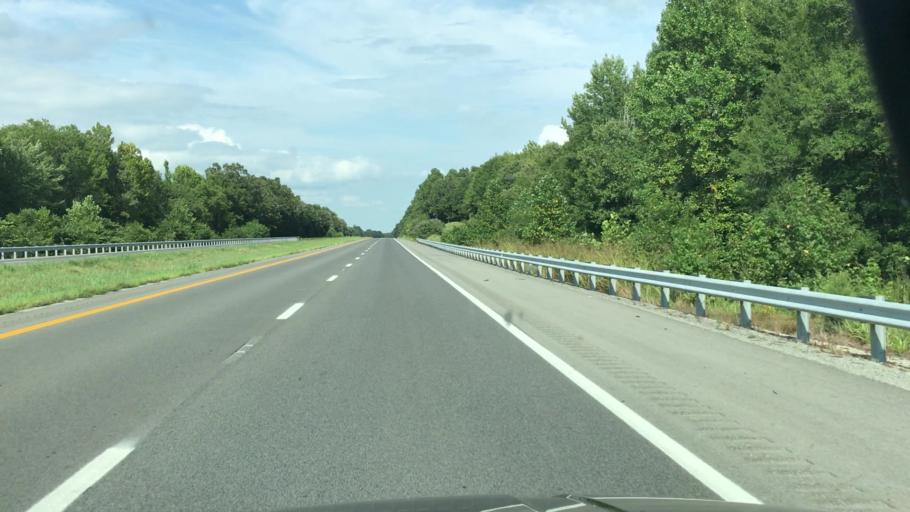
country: US
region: Kentucky
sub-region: Hopkins County
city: Nortonville
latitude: 37.2175
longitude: -87.3943
